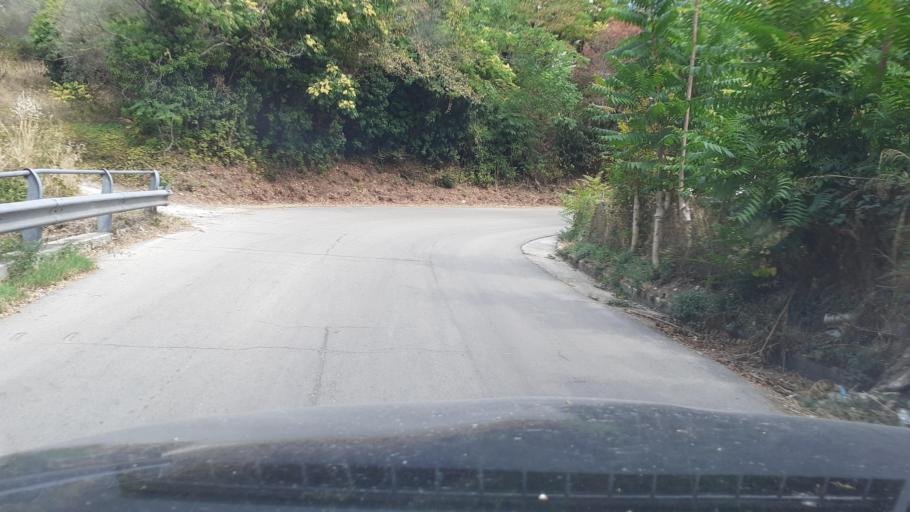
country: IT
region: Abruzzo
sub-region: Provincia di Chieti
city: Fossacesia
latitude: 42.2466
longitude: 14.4793
